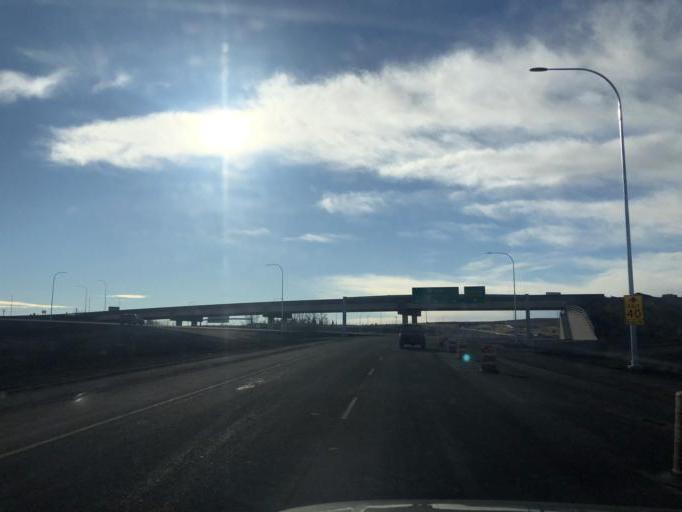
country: CA
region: Alberta
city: Calgary
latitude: 51.0029
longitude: -114.1668
